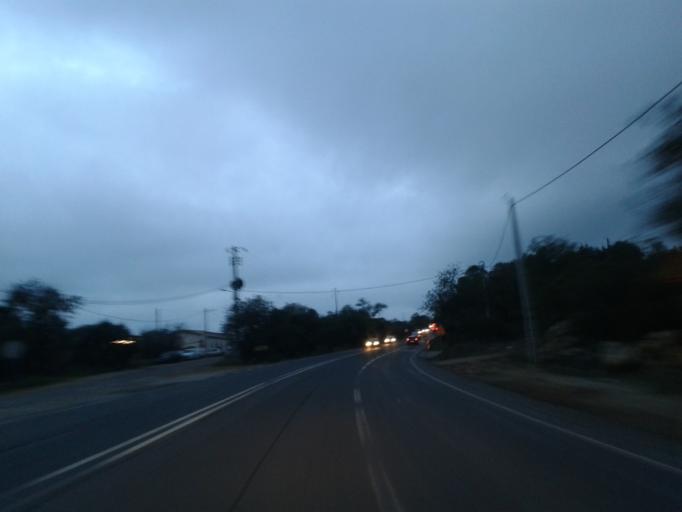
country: PT
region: Faro
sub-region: Albufeira
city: Ferreiras
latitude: 37.1222
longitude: -8.2130
